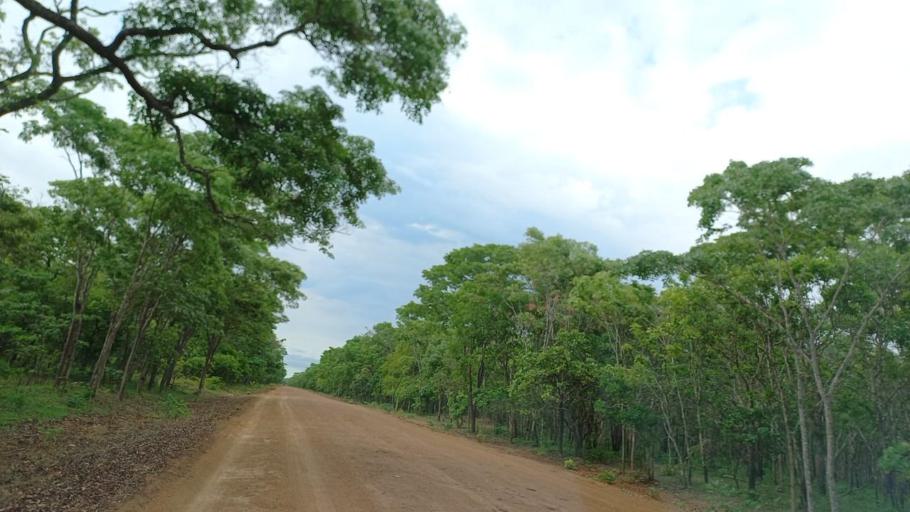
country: ZM
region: North-Western
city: Kalengwa
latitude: -13.3758
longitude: 25.0731
